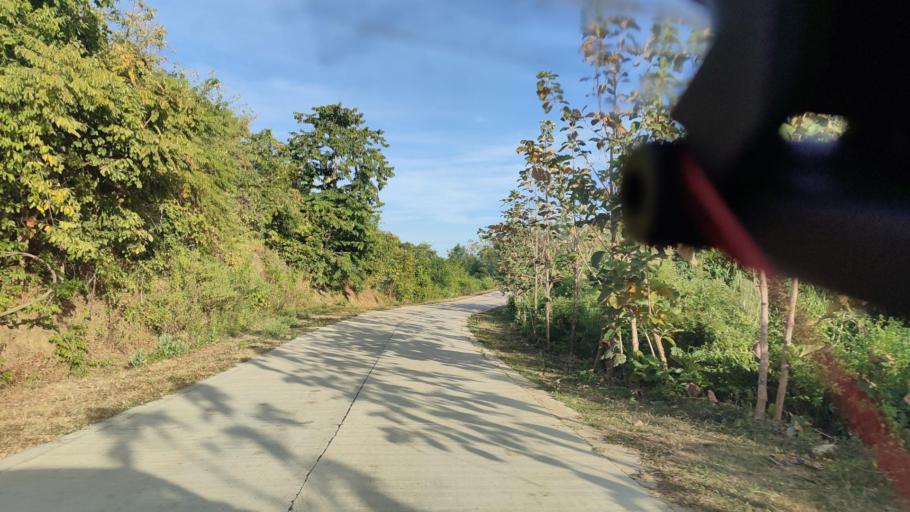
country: MM
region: Magway
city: Taungdwingyi
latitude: 20.0179
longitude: 95.8069
